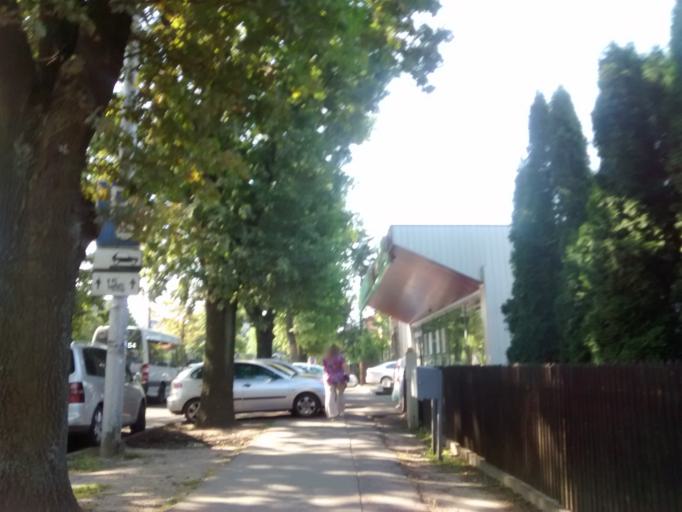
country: LT
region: Kauno apskritis
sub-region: Kaunas
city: Eiguliai
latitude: 54.9168
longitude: 23.9208
